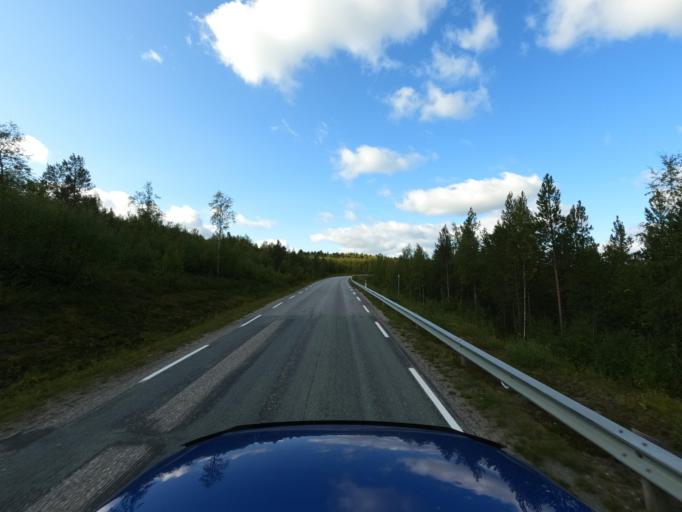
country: NO
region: Finnmark Fylke
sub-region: Karasjok
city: Karasjohka
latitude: 69.4283
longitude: 25.7608
